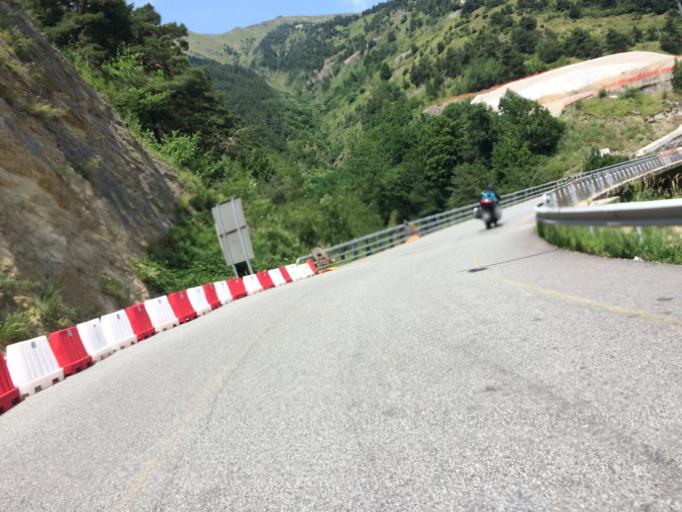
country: FR
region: Provence-Alpes-Cote d'Azur
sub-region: Departement des Alpes-Maritimes
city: Tende
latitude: 44.1356
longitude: 7.5672
